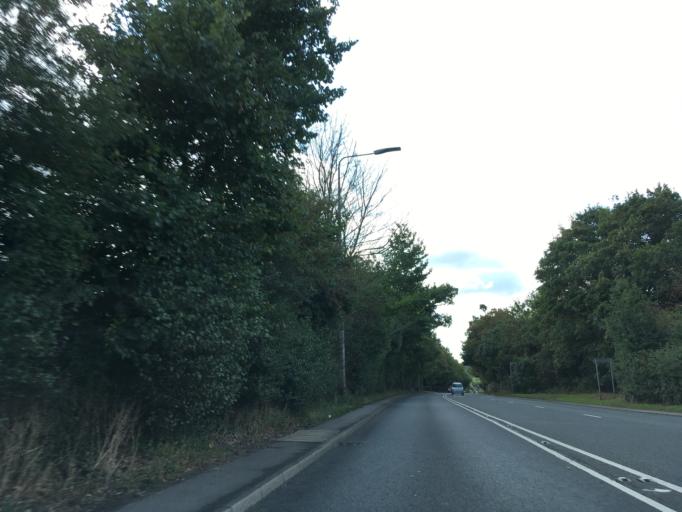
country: GB
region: England
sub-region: West Berkshire
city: Greenham
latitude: 51.3800
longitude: -1.3190
